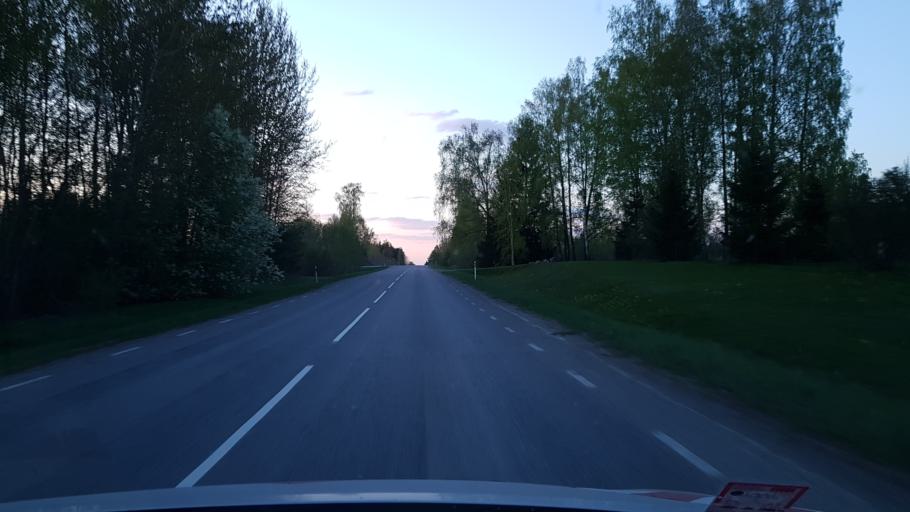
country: EE
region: Vorumaa
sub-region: Voru linn
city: Voru
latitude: 57.7861
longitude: 27.0348
